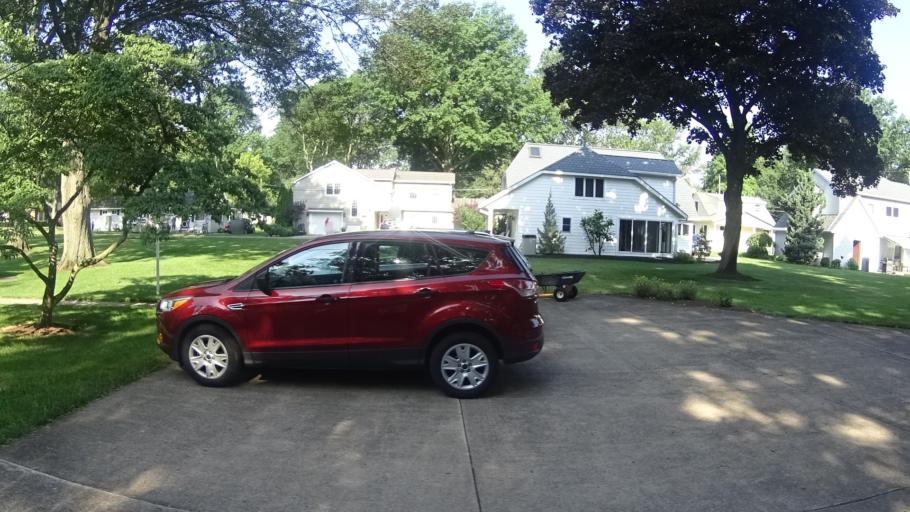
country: US
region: Ohio
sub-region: Lorain County
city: Vermilion
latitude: 41.3877
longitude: -82.4537
